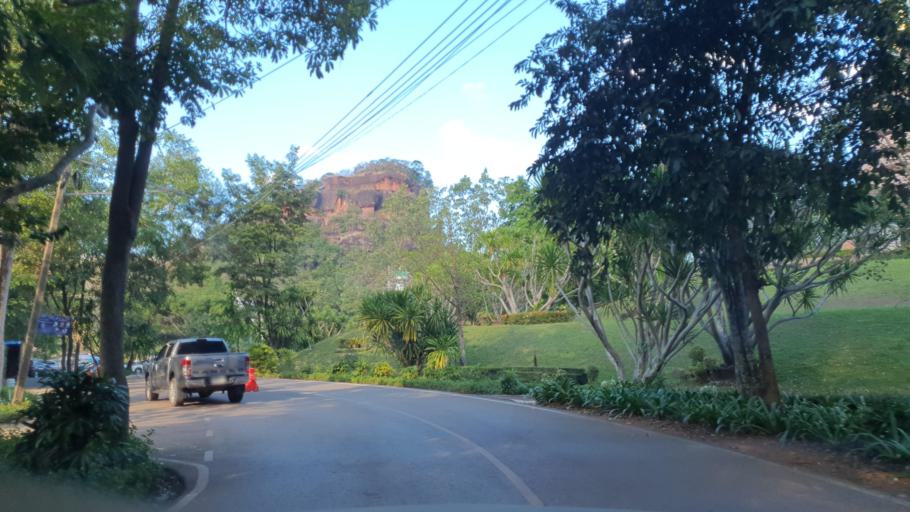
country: TH
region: Changwat Bueng Kan
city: Si Wilai
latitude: 18.1299
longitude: 103.8802
